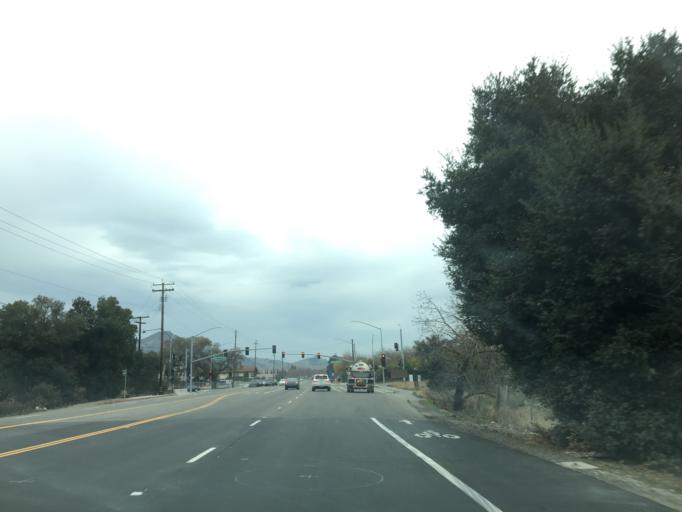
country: US
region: California
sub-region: Santa Clara County
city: Morgan Hill
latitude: 37.1070
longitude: -121.6342
